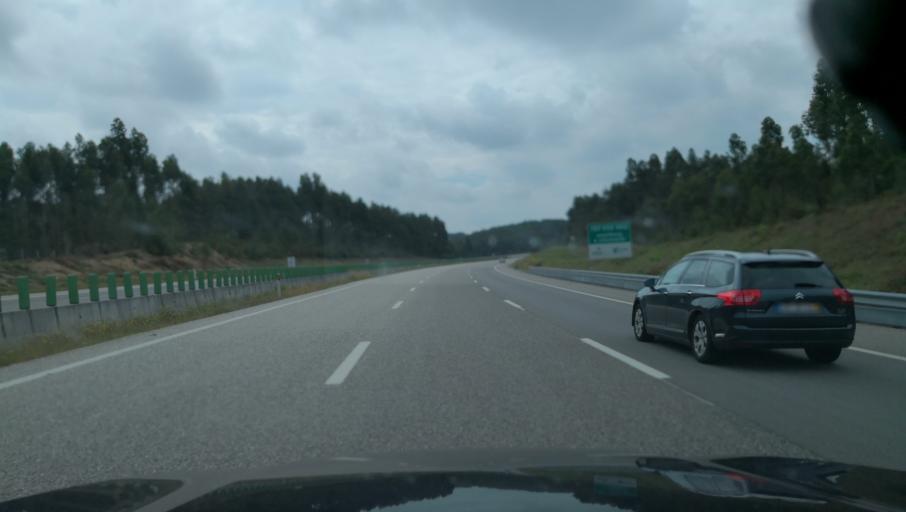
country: PT
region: Leiria
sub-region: Pombal
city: Lourical
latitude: 39.9840
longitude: -8.7883
